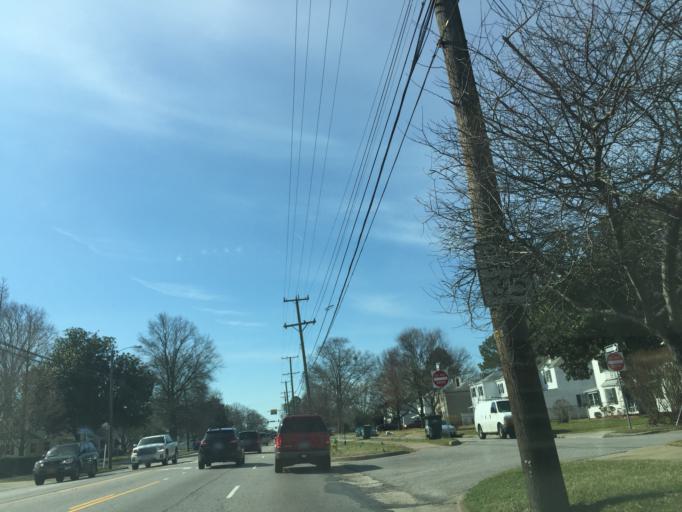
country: US
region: Virginia
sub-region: City of Norfolk
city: Norfolk
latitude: 36.8855
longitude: -76.2606
